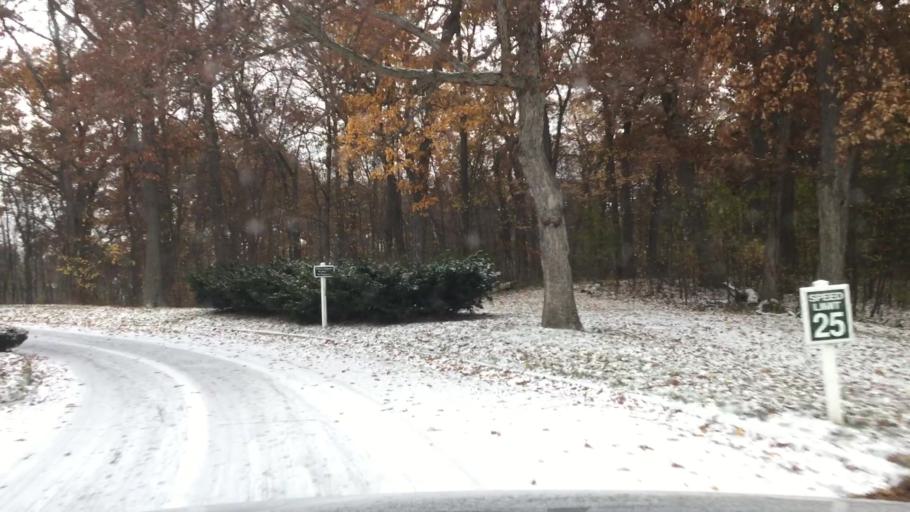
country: US
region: Michigan
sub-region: Livingston County
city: Brighton
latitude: 42.5288
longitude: -83.8510
